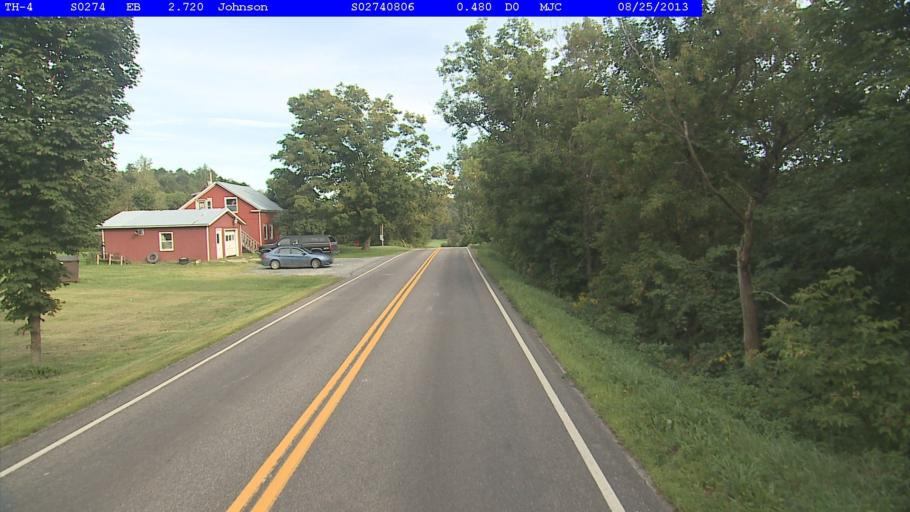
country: US
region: Vermont
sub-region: Lamoille County
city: Johnson
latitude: 44.6543
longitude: -72.7419
